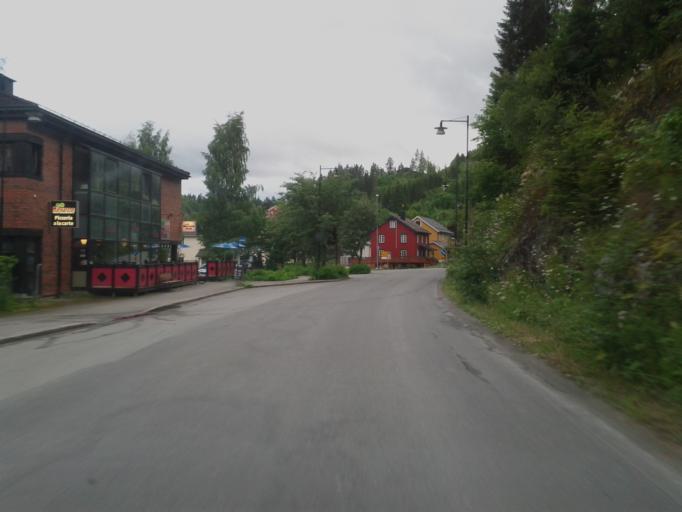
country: NO
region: Sor-Trondelag
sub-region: Midtre Gauldal
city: Storen
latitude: 63.0474
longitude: 10.2824
